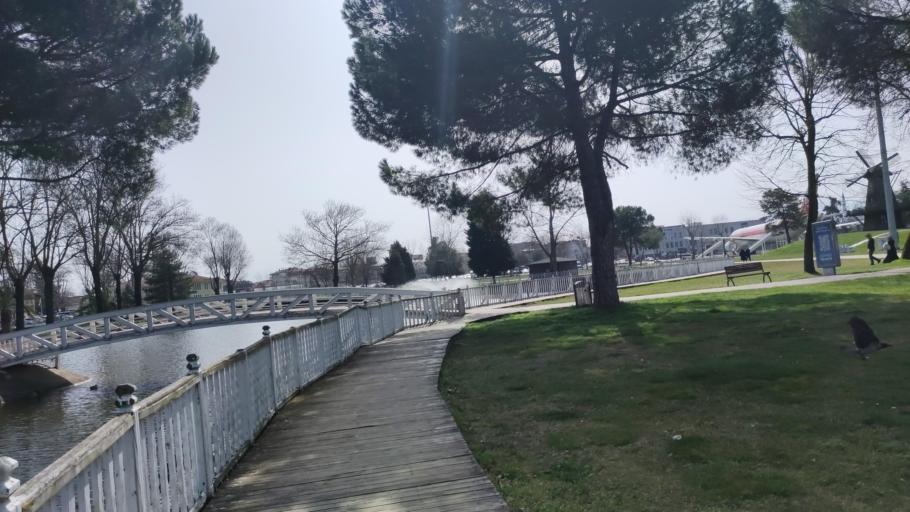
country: TR
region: Sakarya
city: Adapazari
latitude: 40.7716
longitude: 30.3880
